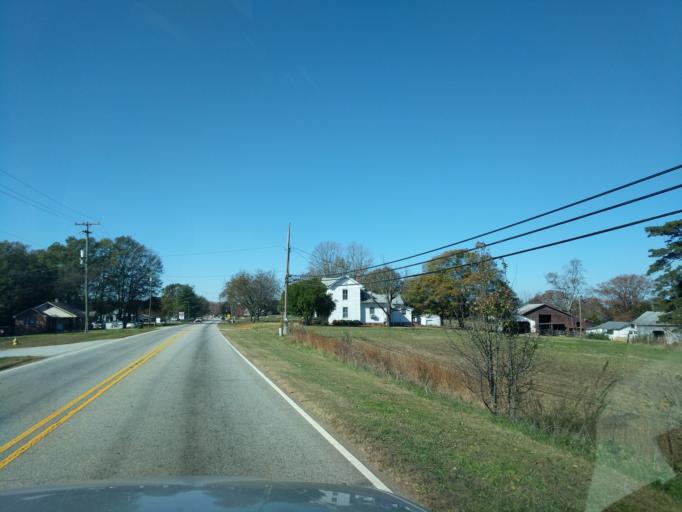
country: US
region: South Carolina
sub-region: Greenville County
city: Taylors
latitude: 34.9516
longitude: -82.2802
